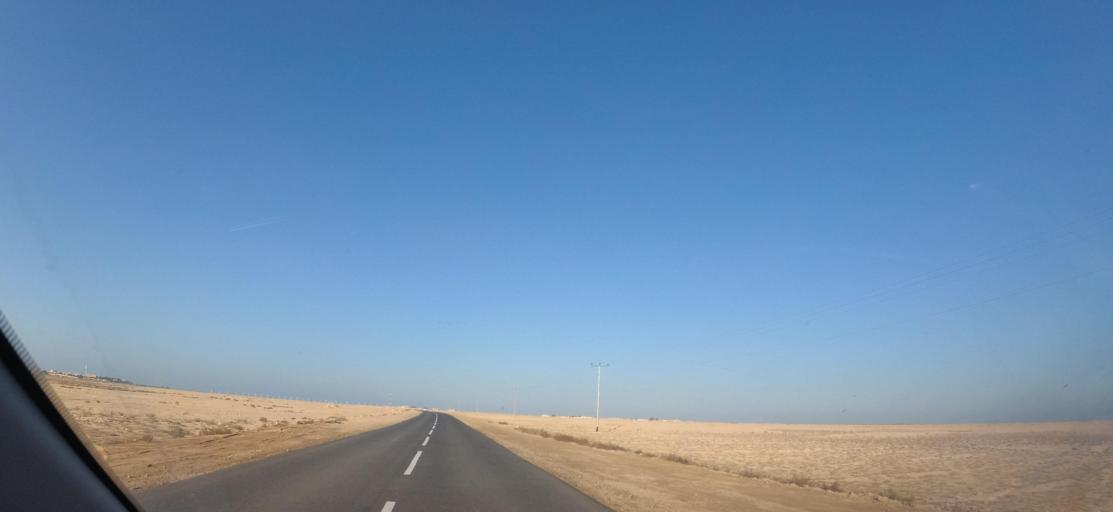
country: QA
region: Madinat ash Shamal
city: Ar Ru'ays
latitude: 26.1421
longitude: 51.2448
